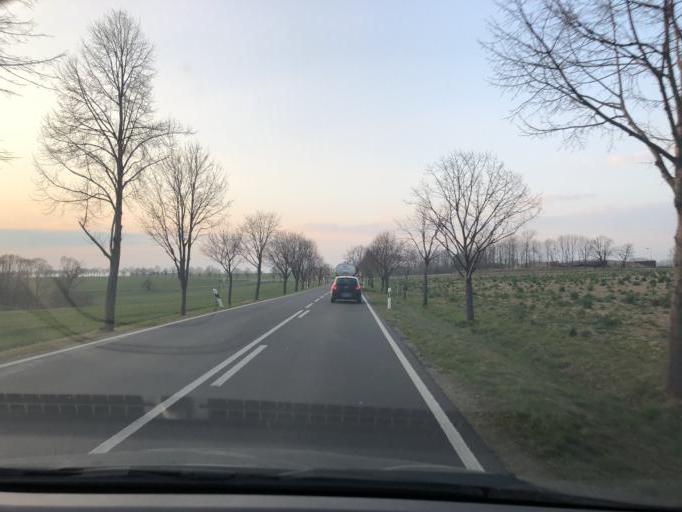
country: DE
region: Saxony
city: Goda
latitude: 51.2110
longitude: 14.2875
